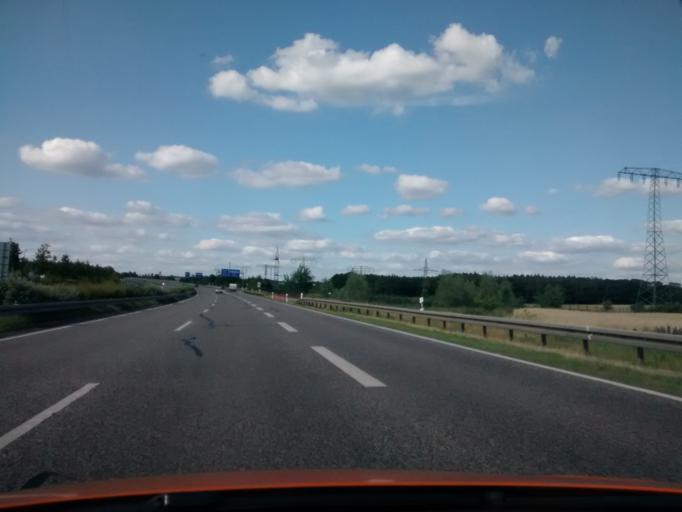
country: DE
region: Brandenburg
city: Ludwigsfelde
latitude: 52.3011
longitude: 13.2856
